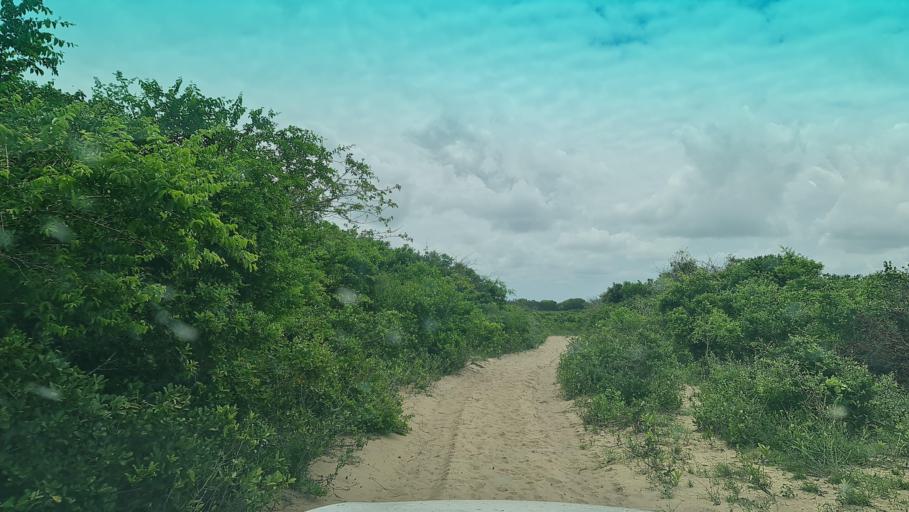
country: MZ
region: Maputo
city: Manhica
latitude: -25.6240
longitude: 32.7773
